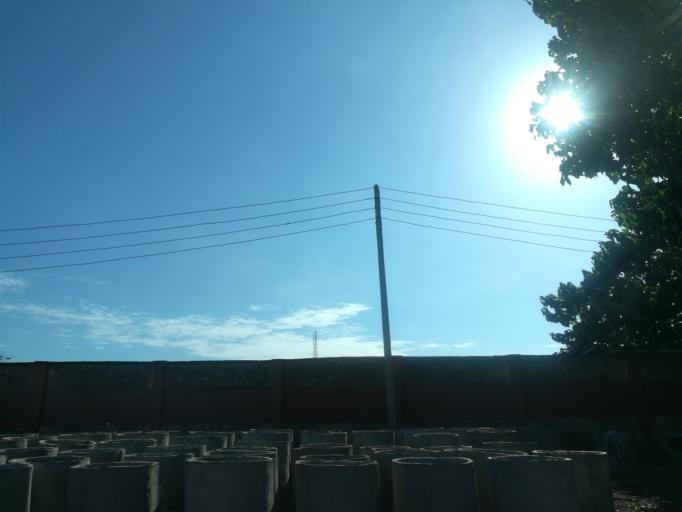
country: NG
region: Lagos
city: Ebute Ikorodu
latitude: 6.5524
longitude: 3.5396
